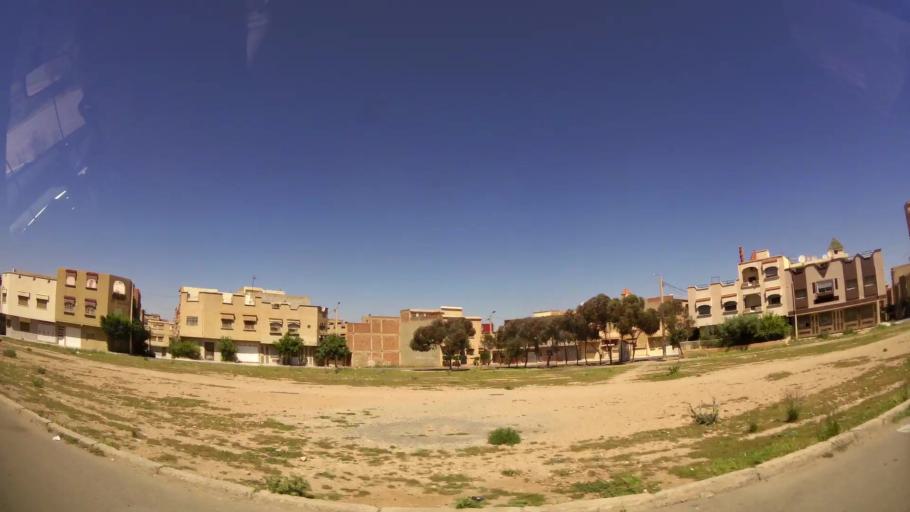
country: MA
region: Oriental
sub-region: Oujda-Angad
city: Oujda
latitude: 34.6611
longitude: -1.8762
